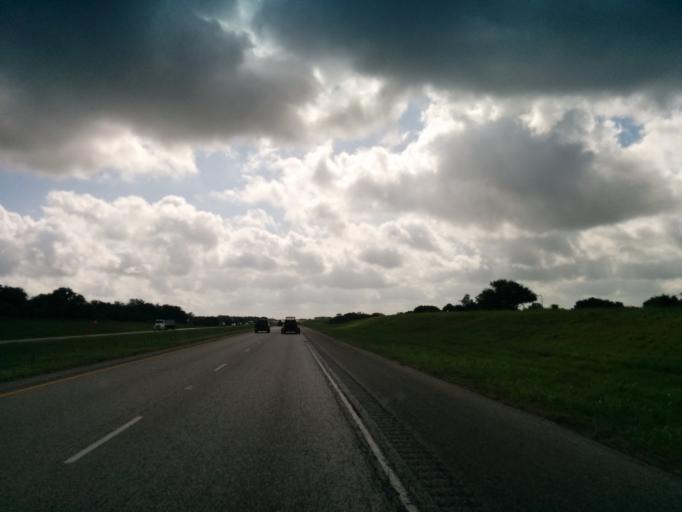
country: US
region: Texas
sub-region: Gonzales County
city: Waelder
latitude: 29.6629
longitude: -97.3765
